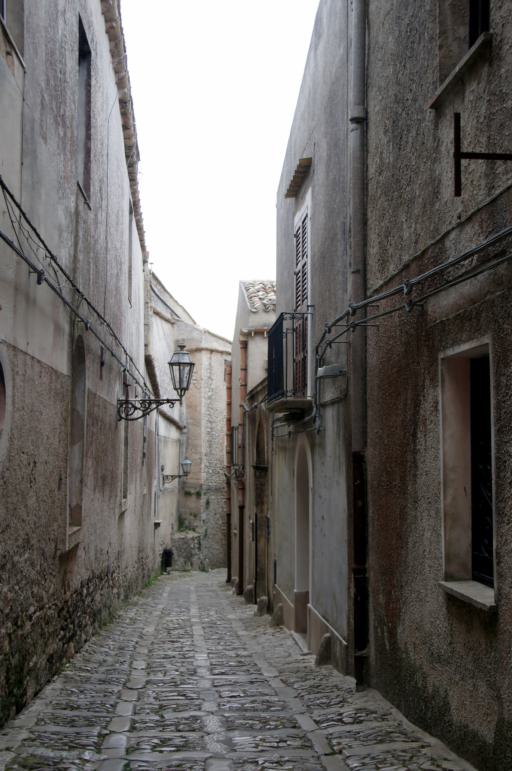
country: IT
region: Sicily
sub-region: Trapani
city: Erice
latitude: 38.0369
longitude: 12.5883
